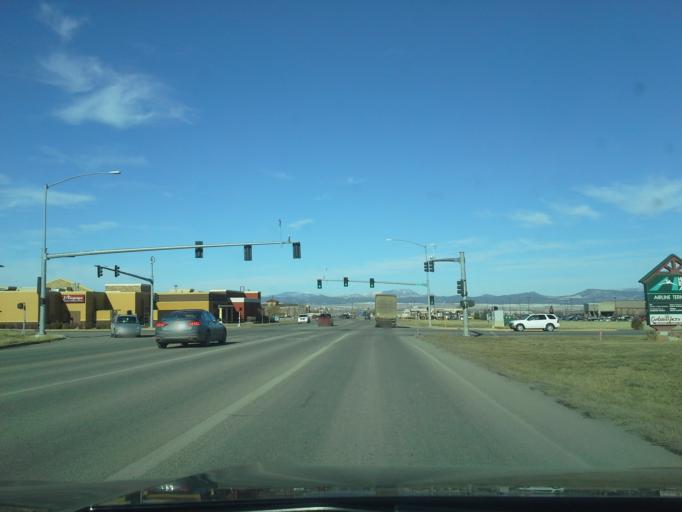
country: US
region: Montana
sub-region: Lewis and Clark County
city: Helena
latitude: 46.6121
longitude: -112.0047
